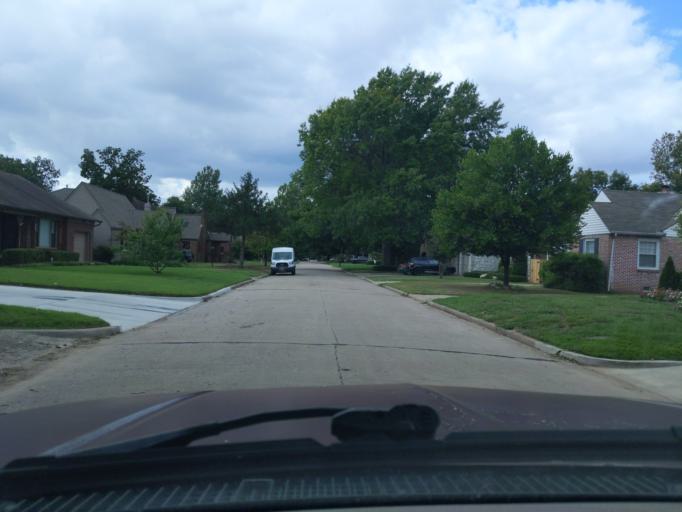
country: US
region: Oklahoma
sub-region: Tulsa County
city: Tulsa
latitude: 36.1107
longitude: -95.9792
